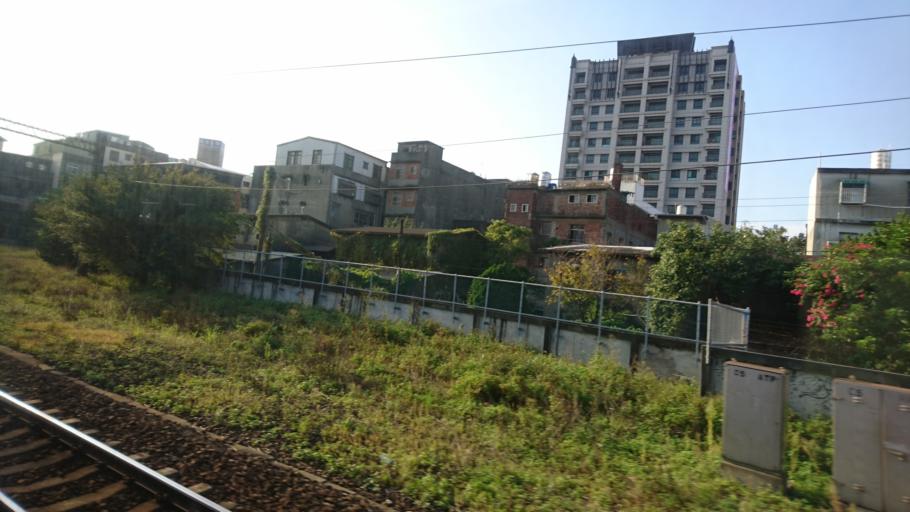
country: TW
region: Taiwan
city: Taoyuan City
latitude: 24.9518
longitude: 121.2222
